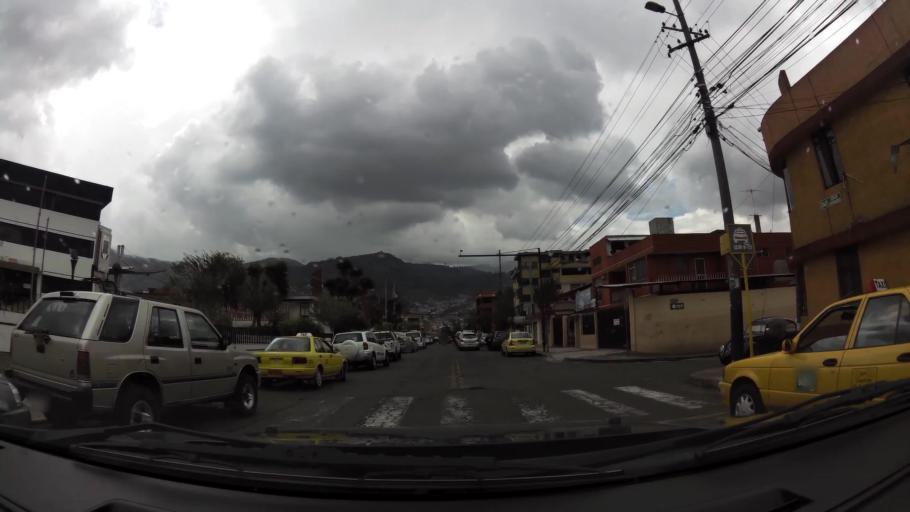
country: EC
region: Pichincha
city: Quito
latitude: -0.2484
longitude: -78.5245
